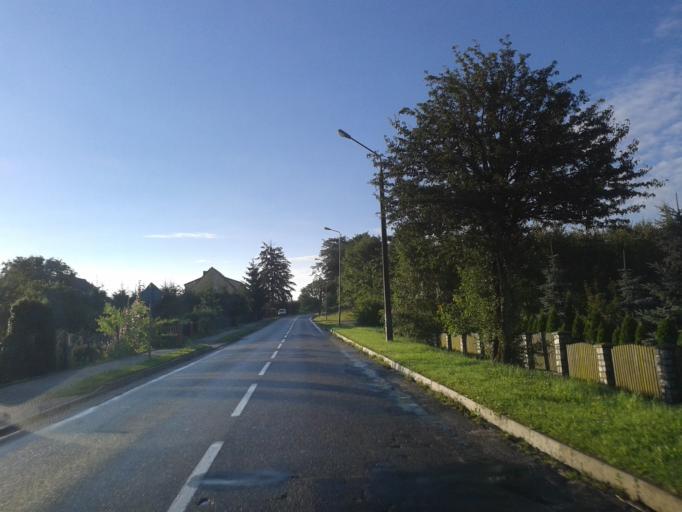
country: PL
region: West Pomeranian Voivodeship
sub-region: Powiat szczecinecki
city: Barwice
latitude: 53.7361
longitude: 16.3600
